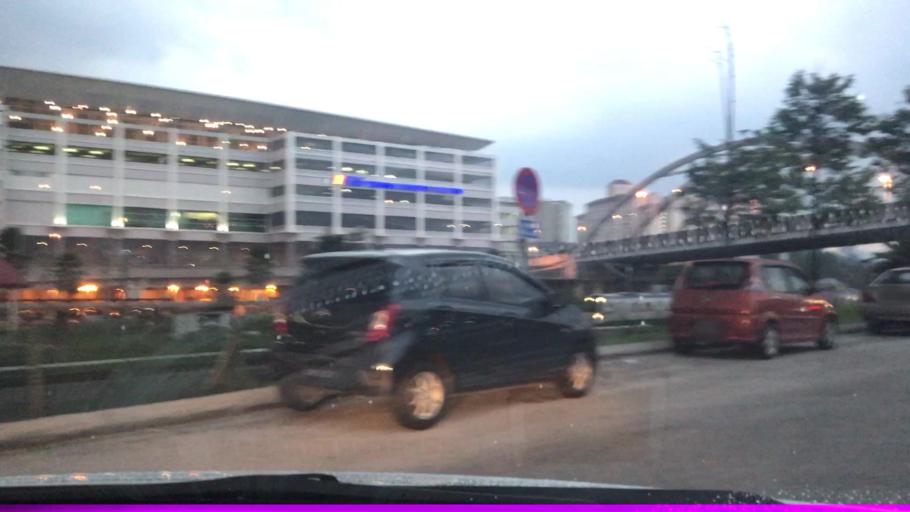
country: MY
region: Selangor
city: Kampong Baharu Balakong
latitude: 3.0762
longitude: 101.7117
